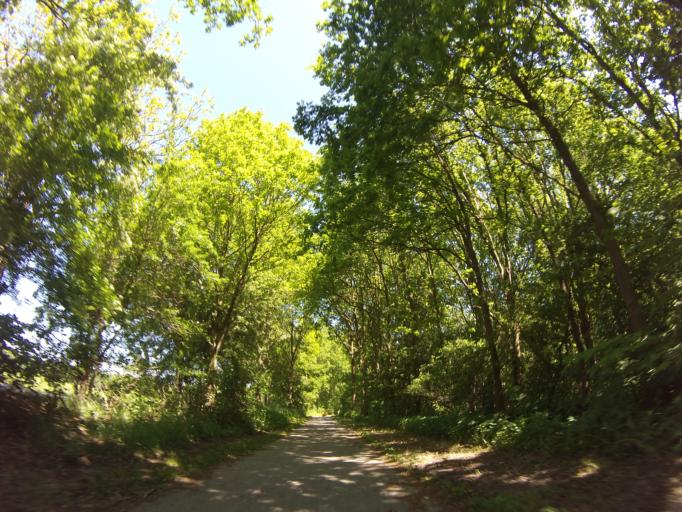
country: NL
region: Drenthe
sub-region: Gemeente Hoogeveen
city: Hoogeveen
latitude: 52.7958
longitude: 6.5162
